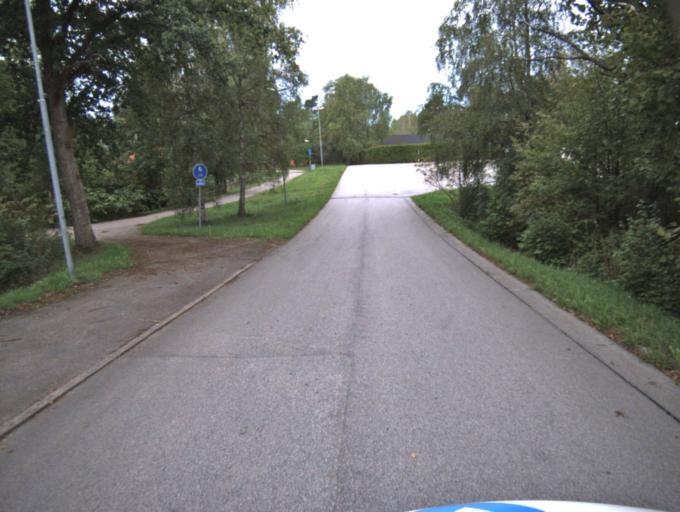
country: SE
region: Vaestra Goetaland
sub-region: Ulricehamns Kommun
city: Ulricehamn
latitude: 57.7862
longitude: 13.4255
